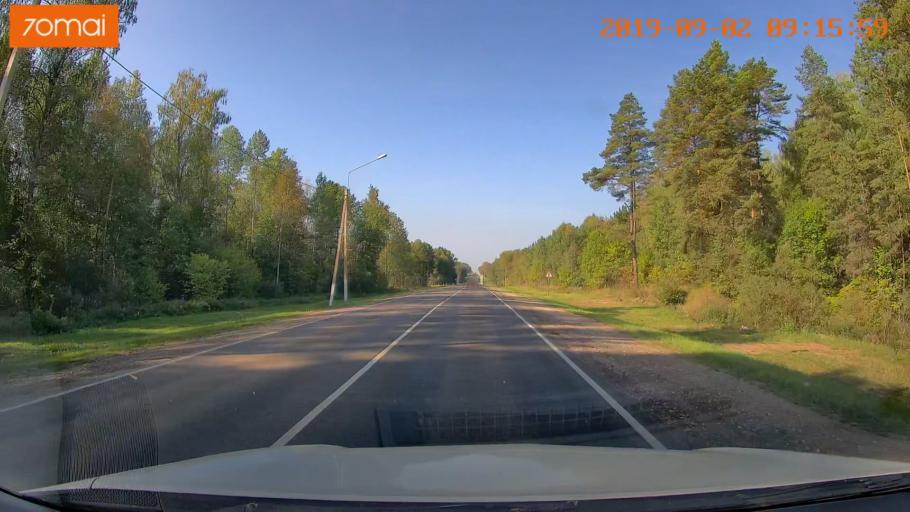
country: RU
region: Kaluga
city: Nikola-Lenivets
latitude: 54.8354
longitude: 35.4837
